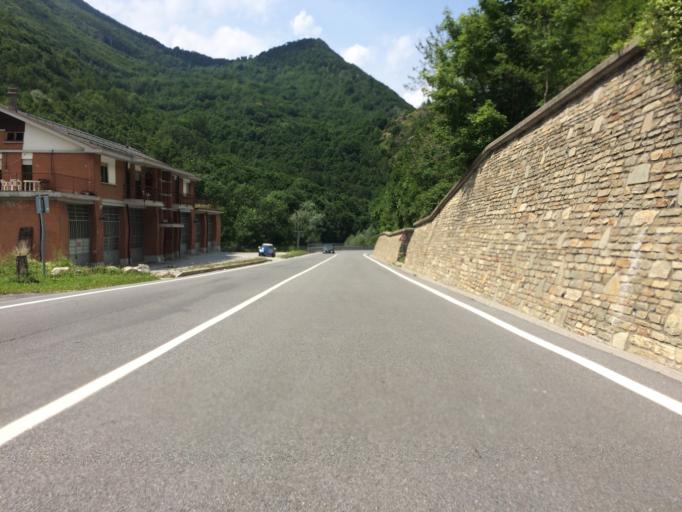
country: IT
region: Piedmont
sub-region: Provincia di Cuneo
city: Limone Piemonte
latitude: 44.2088
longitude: 7.5737
